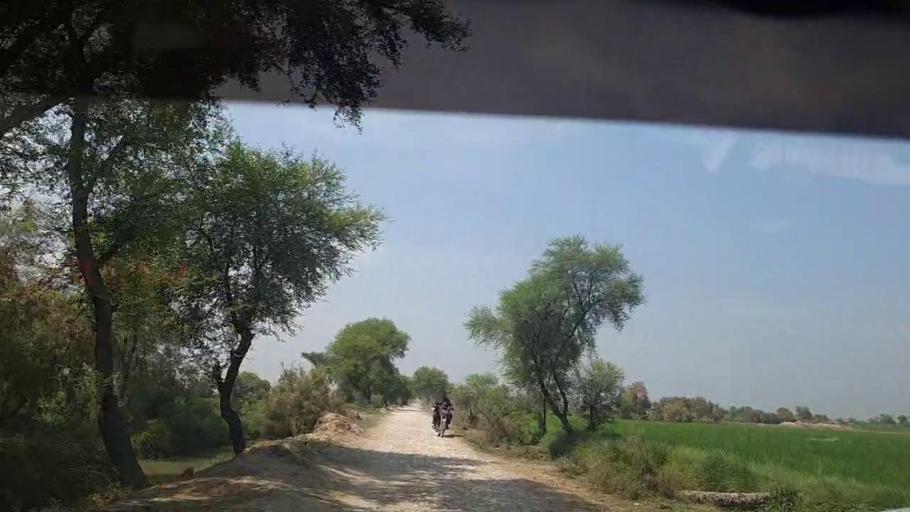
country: PK
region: Sindh
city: Thul
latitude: 28.2052
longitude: 68.6945
